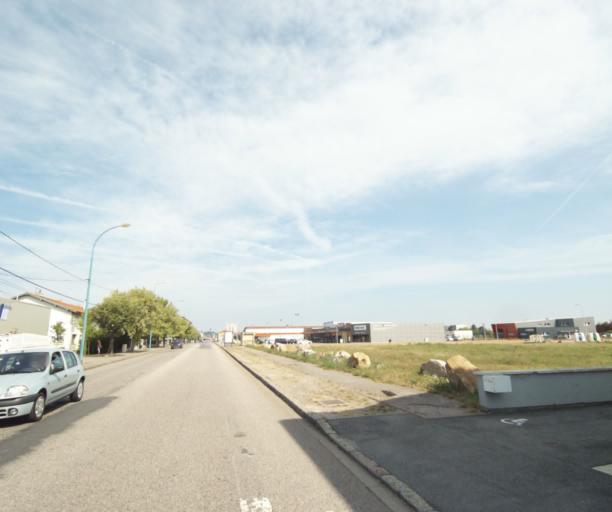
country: FR
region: Lorraine
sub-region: Departement de Meurthe-et-Moselle
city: Luneville
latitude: 48.5848
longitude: 6.5130
